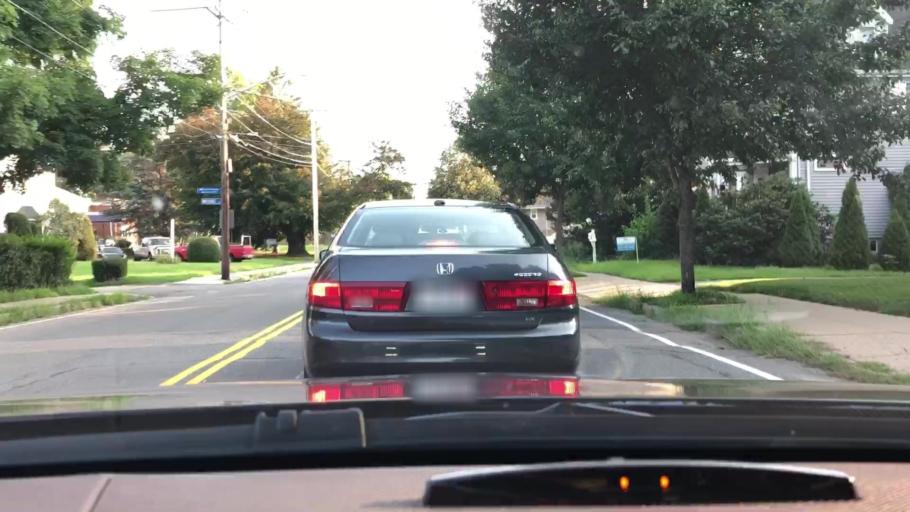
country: US
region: Massachusetts
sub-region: Norfolk County
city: Norwood
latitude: 42.1990
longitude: -71.1981
